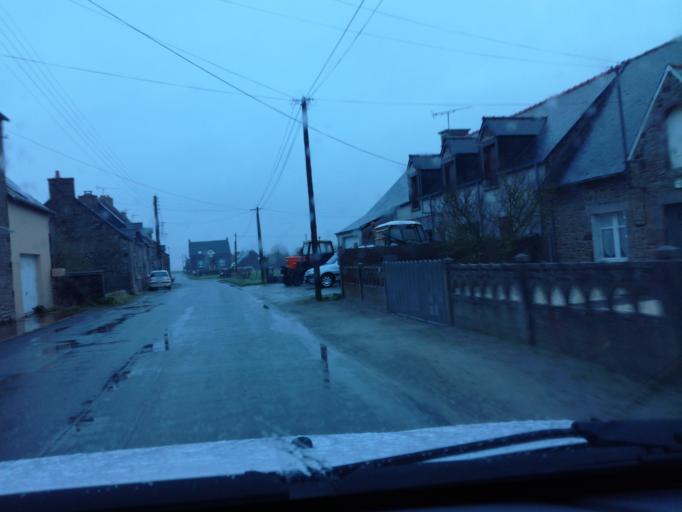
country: FR
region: Brittany
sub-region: Departement d'Ille-et-Vilaine
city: Cherrueix
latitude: 48.6100
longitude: -1.6801
